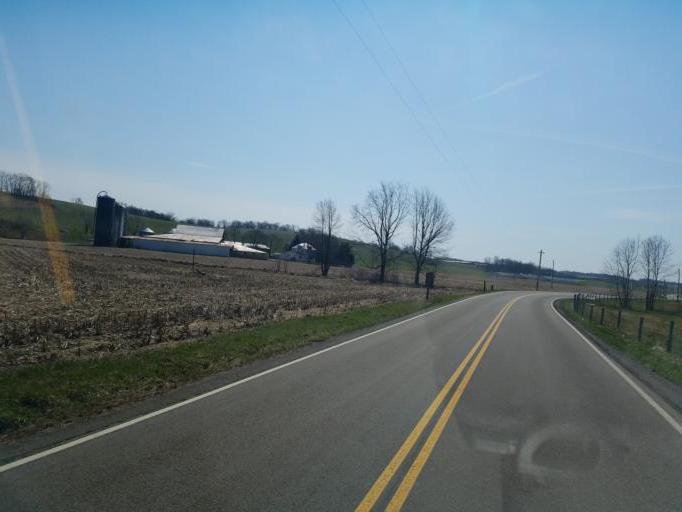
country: US
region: Ohio
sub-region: Knox County
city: Danville
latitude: 40.4949
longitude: -82.2860
